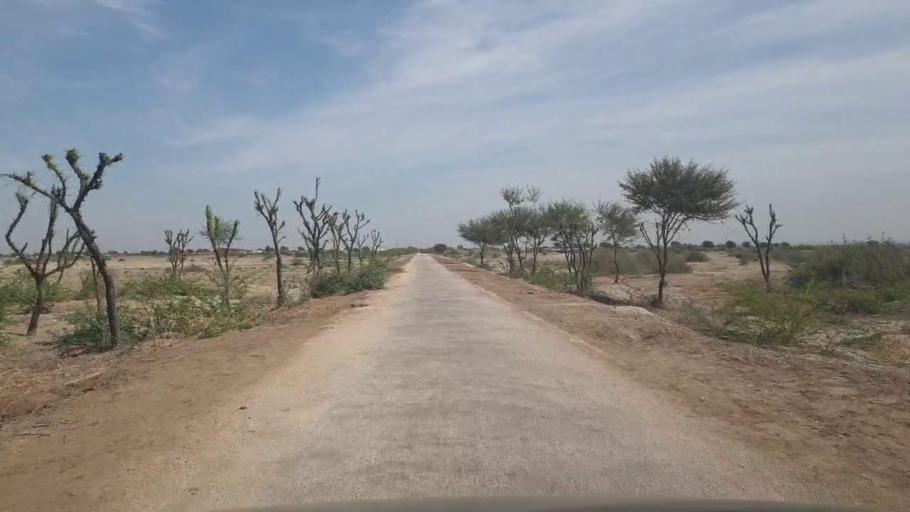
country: PK
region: Sindh
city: Kunri
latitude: 25.2125
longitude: 69.6240
